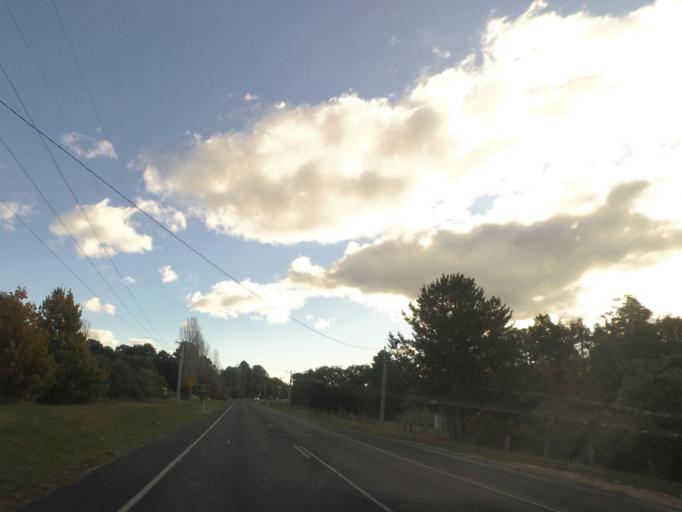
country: AU
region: Victoria
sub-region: Mount Alexander
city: Castlemaine
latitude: -37.0851
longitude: 144.2746
